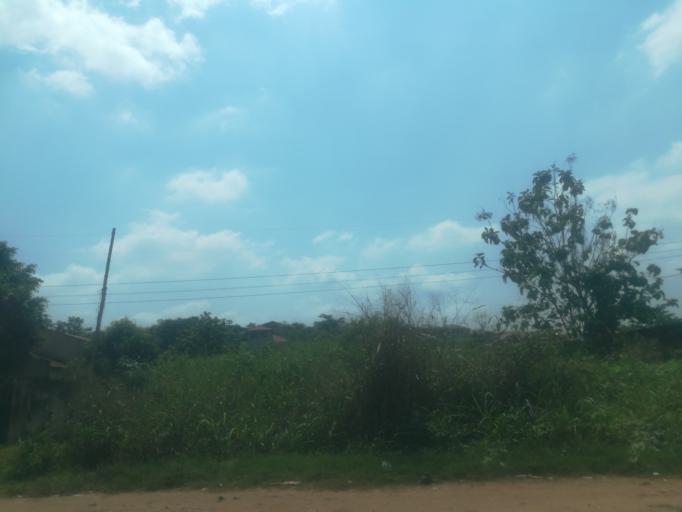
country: NG
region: Ogun
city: Abeokuta
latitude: 7.1425
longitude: 3.3902
